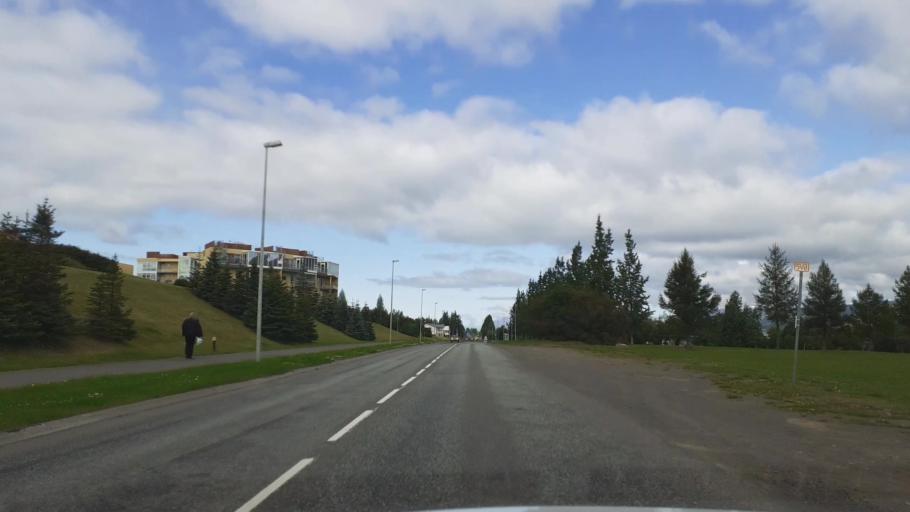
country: IS
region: Northeast
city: Akureyri
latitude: 65.6713
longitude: -18.0957
